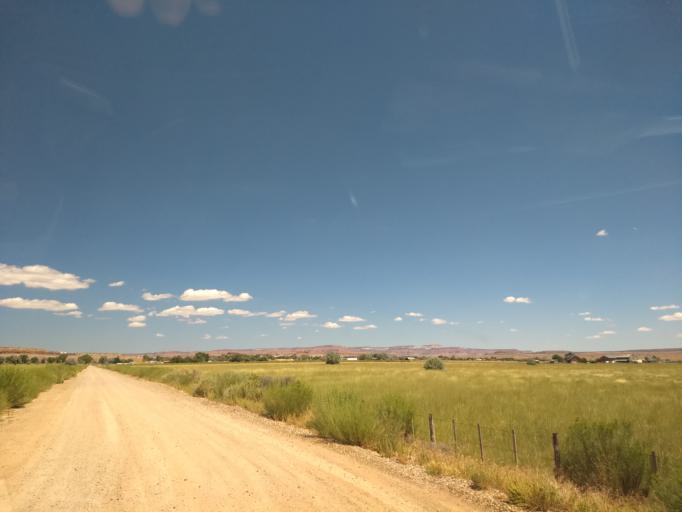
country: US
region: Arizona
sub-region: Coconino County
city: Fredonia
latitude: 36.9253
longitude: -112.5399
